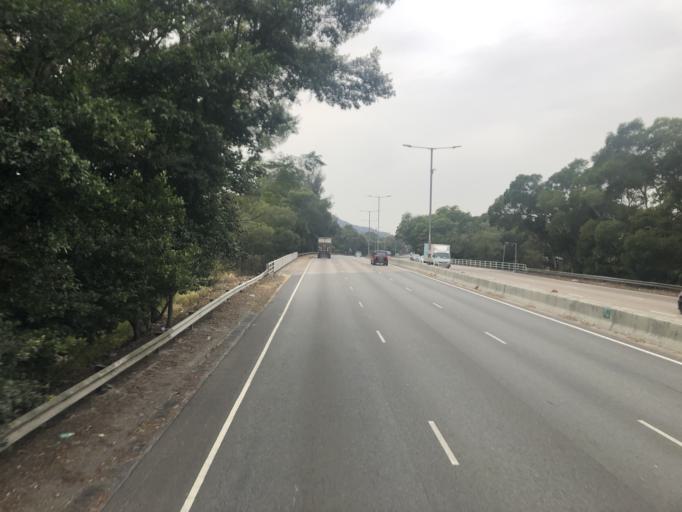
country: CN
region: Guangdong
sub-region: Shenzhen
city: Shenzhen
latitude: 22.5022
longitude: 114.1171
